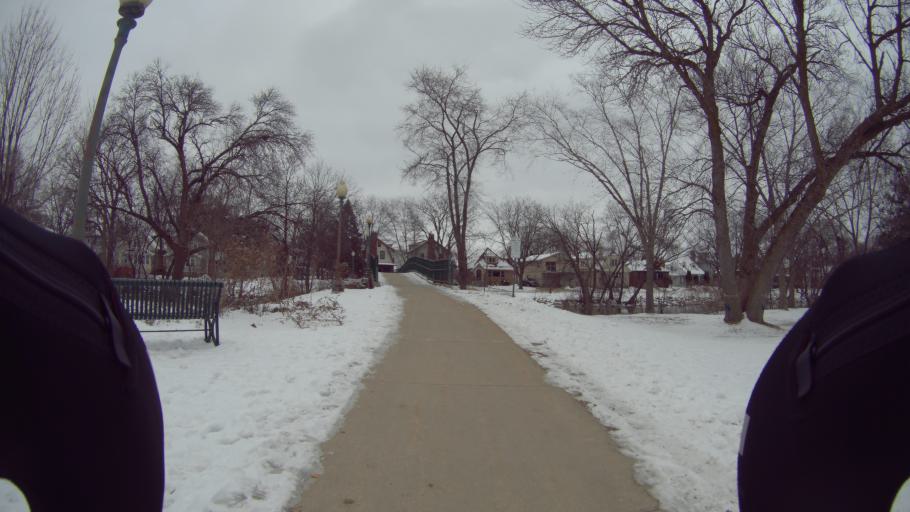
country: US
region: Wisconsin
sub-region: Dane County
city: Monona
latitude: 43.0871
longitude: -89.3569
